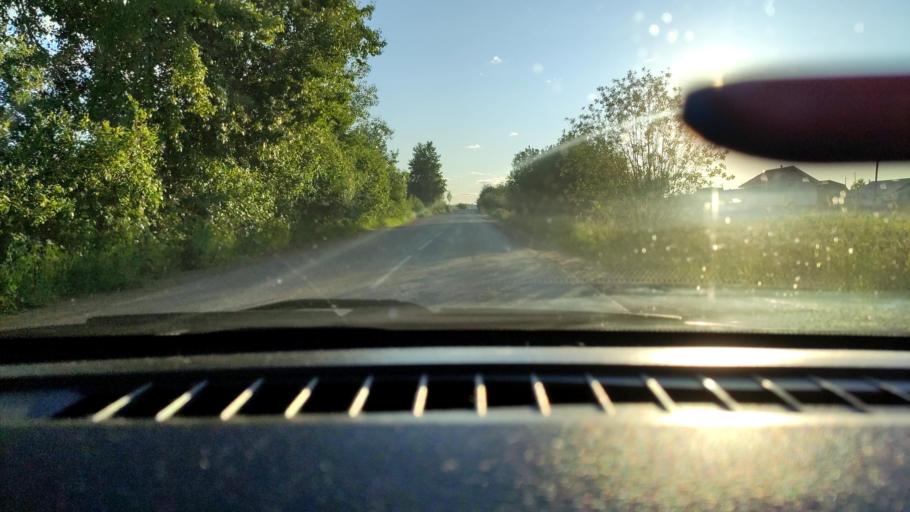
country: RU
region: Perm
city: Kultayevo
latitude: 57.9281
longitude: 55.8728
